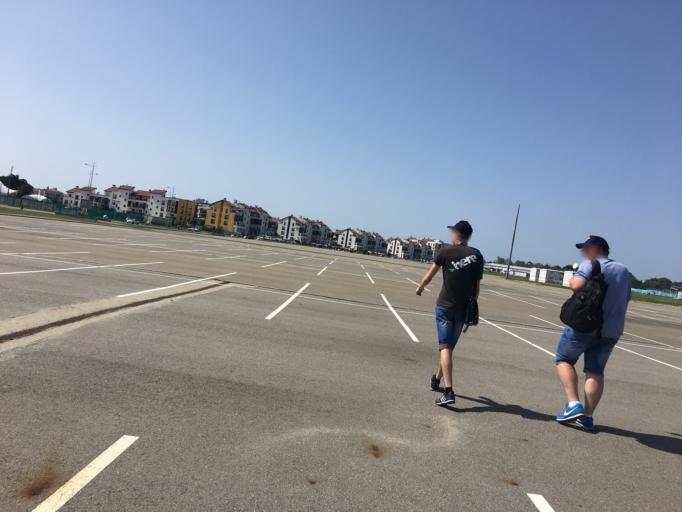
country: RU
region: Krasnodarskiy
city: Adler
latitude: 43.4118
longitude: 39.9474
